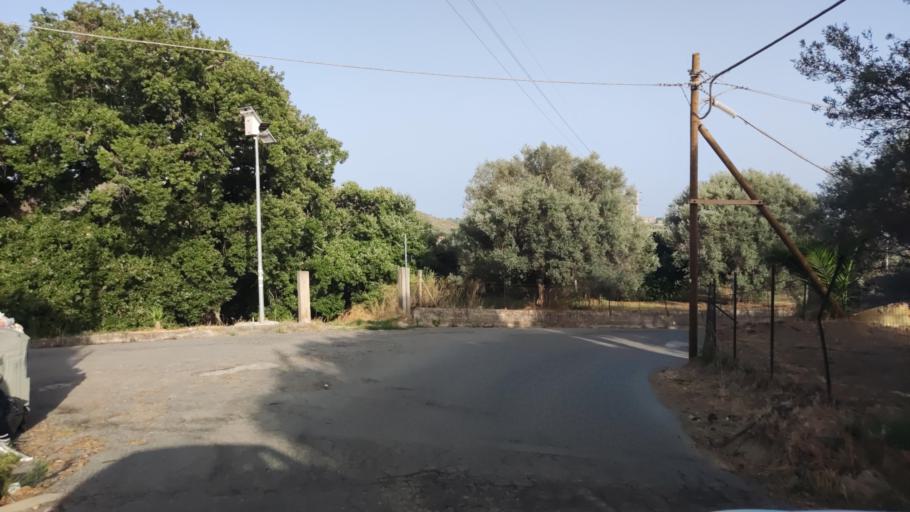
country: IT
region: Calabria
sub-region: Provincia di Reggio Calabria
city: Placanica
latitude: 38.4314
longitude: 16.4530
